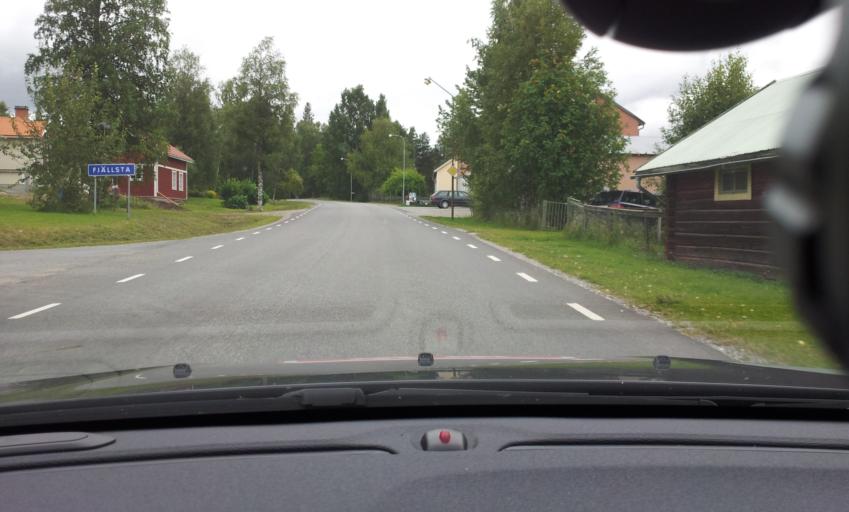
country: SE
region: Jaemtland
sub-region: Braecke Kommun
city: Braecke
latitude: 62.9714
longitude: 15.1691
